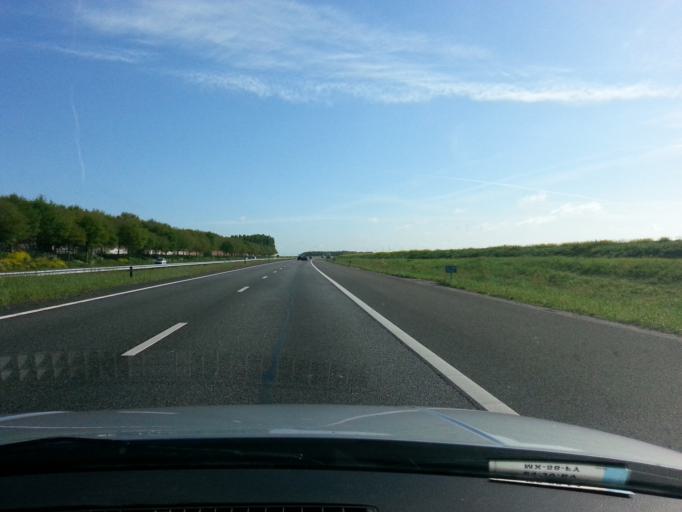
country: NL
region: North Holland
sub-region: Gemeente Blaricum
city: Blaricum
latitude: 52.2845
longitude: 5.2746
